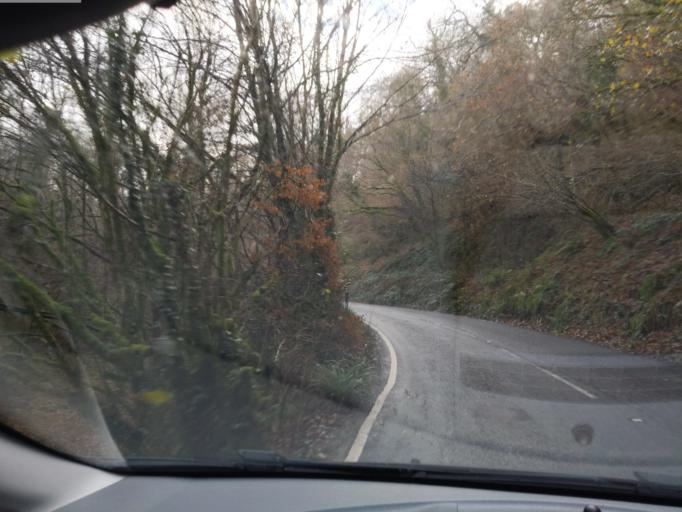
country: GB
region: England
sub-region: Cornwall
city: Looe
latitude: 50.3858
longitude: -4.3901
